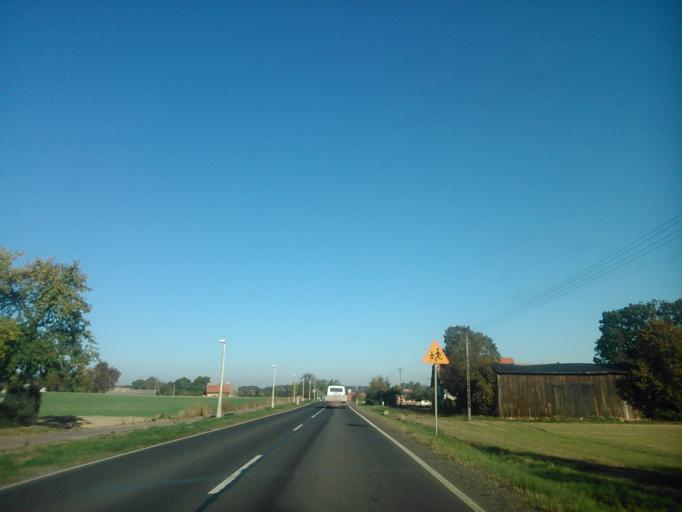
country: PL
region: Kujawsko-Pomorskie
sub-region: Powiat wabrzeski
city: Debowa Laka
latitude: 53.1962
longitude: 19.0387
